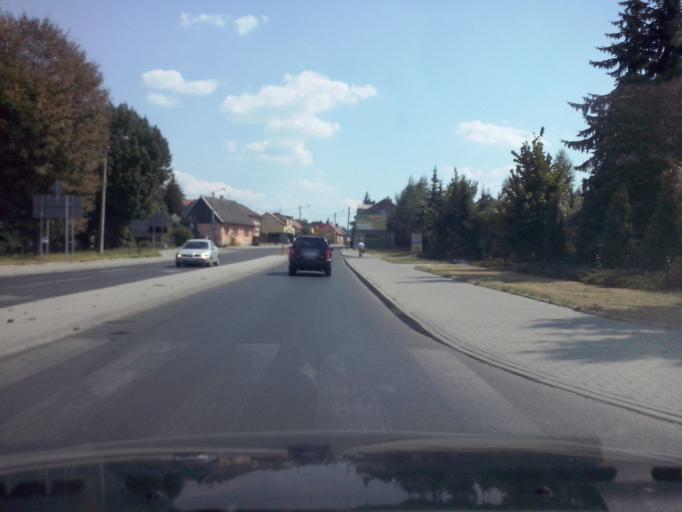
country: PL
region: Swietokrzyskie
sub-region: Powiat staszowski
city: Staszow
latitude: 50.5578
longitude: 21.1620
